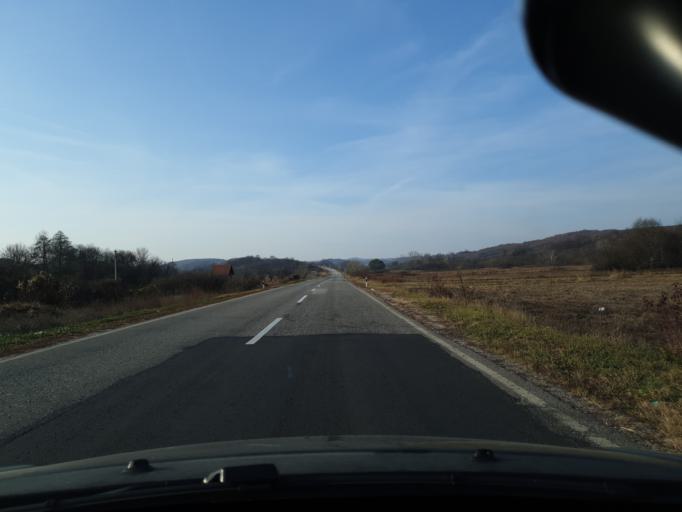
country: RS
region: Central Serbia
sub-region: Zajecarski Okrug
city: Zajecar
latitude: 43.9527
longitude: 22.2818
